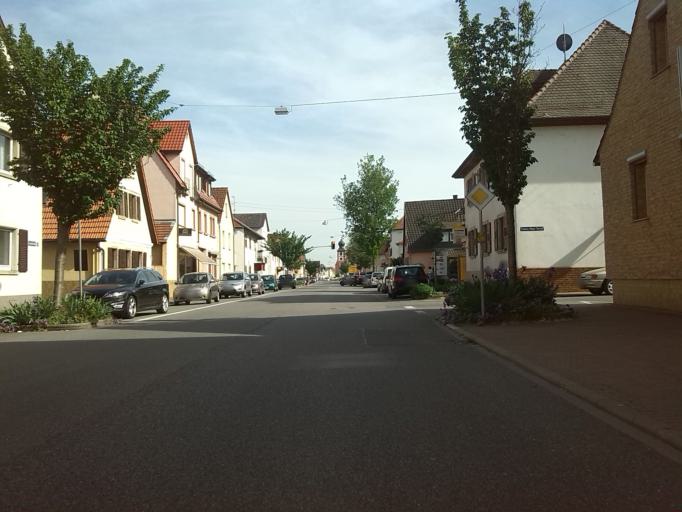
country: DE
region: Baden-Wuerttemberg
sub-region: Karlsruhe Region
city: Edingen-Neckarhausen
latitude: 49.4663
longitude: 8.6004
